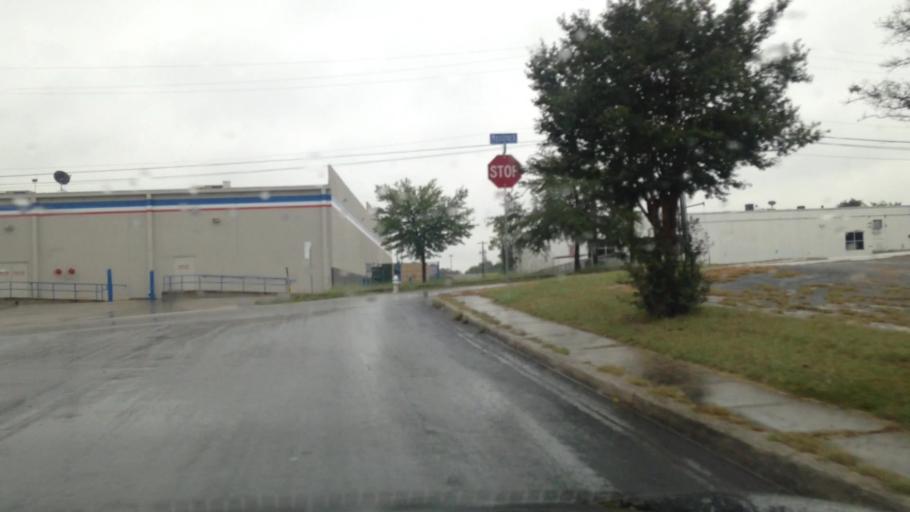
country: US
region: Texas
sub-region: Bexar County
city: Castle Hills
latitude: 29.5131
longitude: -98.5387
